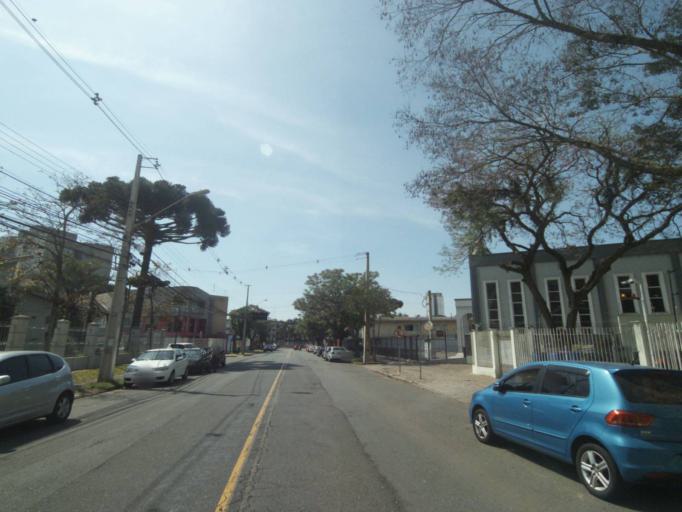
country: BR
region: Parana
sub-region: Curitiba
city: Curitiba
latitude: -25.4737
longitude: -49.2970
